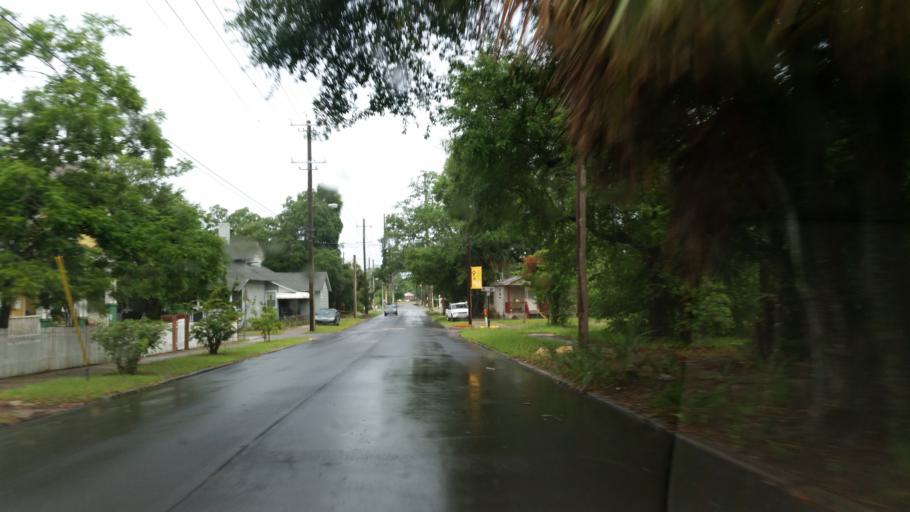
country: US
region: Florida
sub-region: Escambia County
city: Pensacola
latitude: 30.4187
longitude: -87.2214
